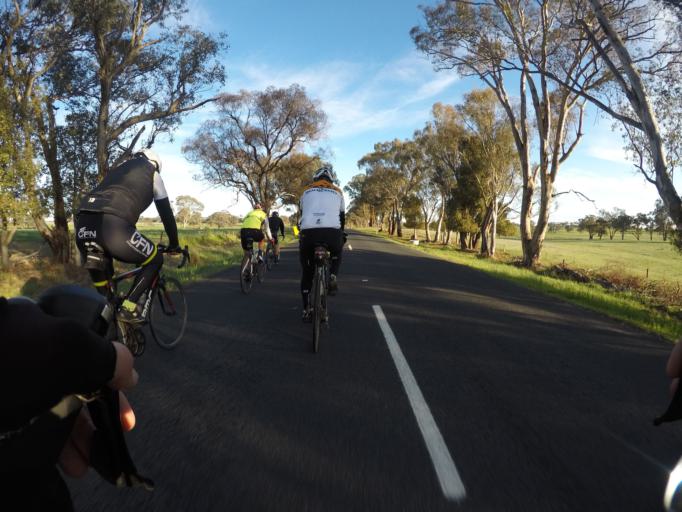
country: AU
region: New South Wales
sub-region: Cabonne
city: Molong
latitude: -33.0289
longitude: 148.8053
